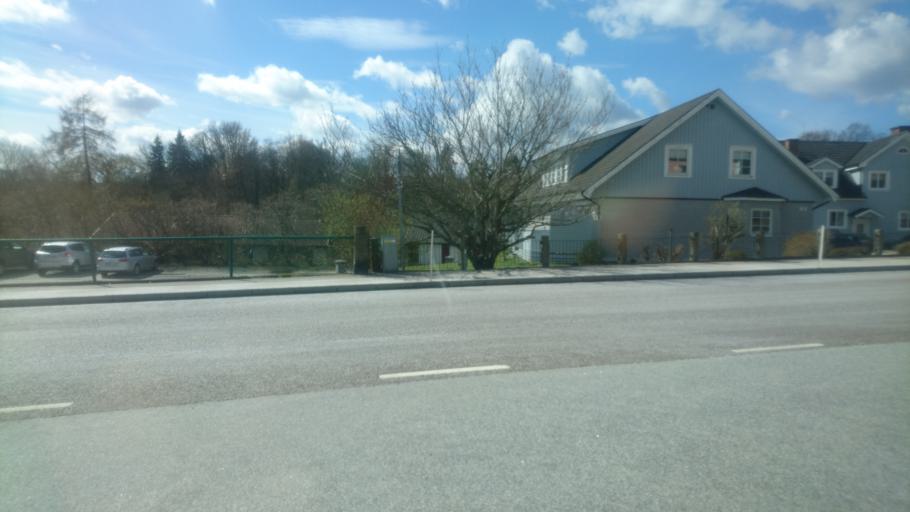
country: SE
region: Blekinge
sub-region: Olofstroms Kommun
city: Jamshog
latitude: 56.2415
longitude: 14.5300
